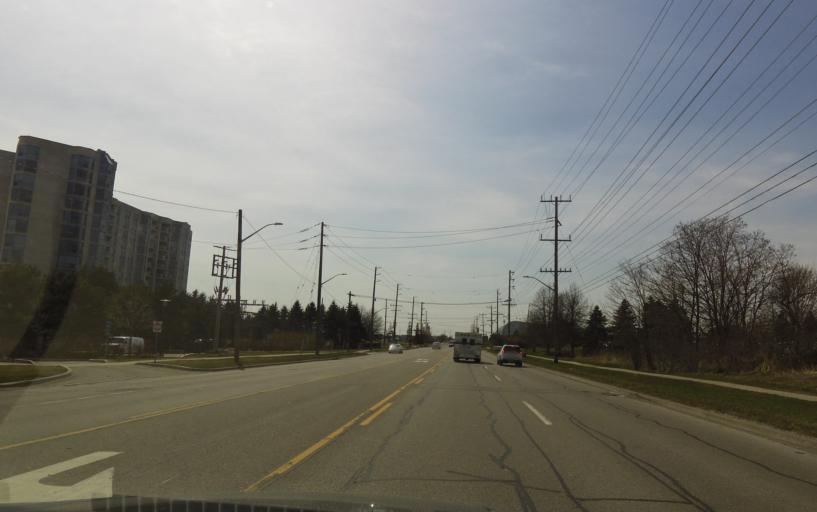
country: CA
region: Ontario
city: Oshawa
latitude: 43.8617
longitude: -78.9373
